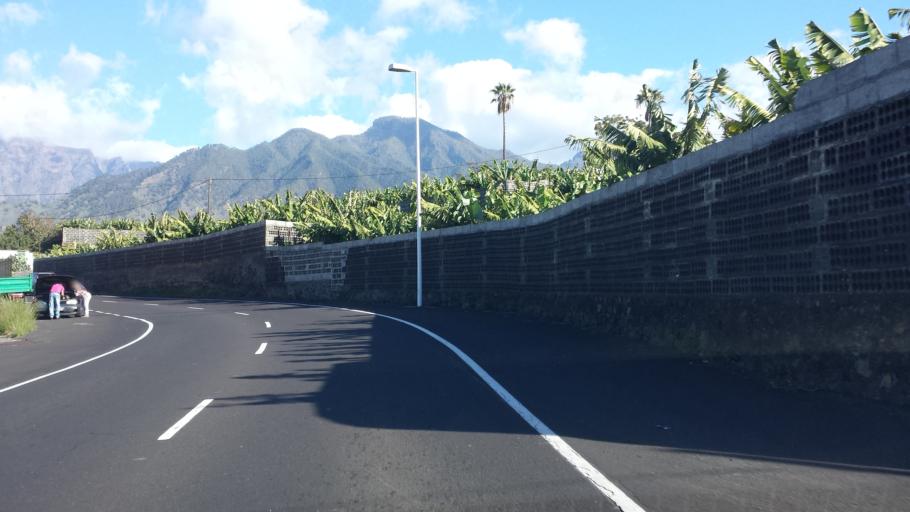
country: ES
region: Canary Islands
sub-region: Provincia de Santa Cruz de Tenerife
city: Los Llanos de Aridane
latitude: 28.6370
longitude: -17.9076
